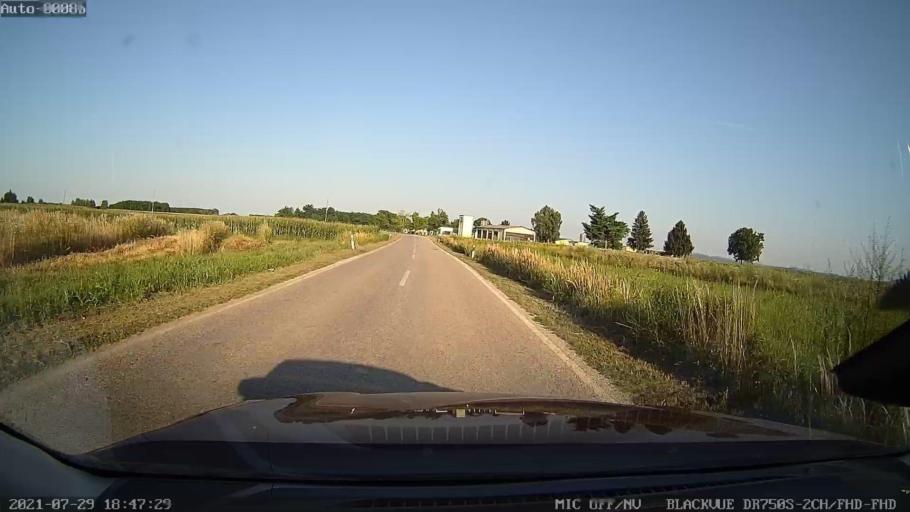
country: HR
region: Varazdinska
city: Sracinec
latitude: 46.3120
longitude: 16.2775
